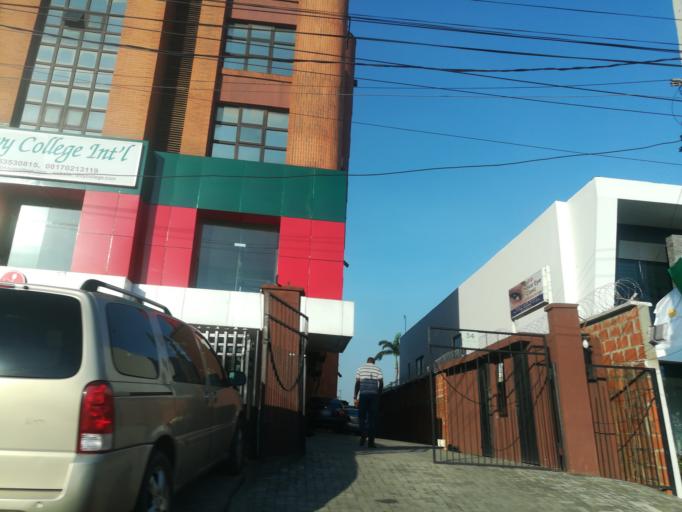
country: NG
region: Lagos
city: Ikeja
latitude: 6.5992
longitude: 3.3532
